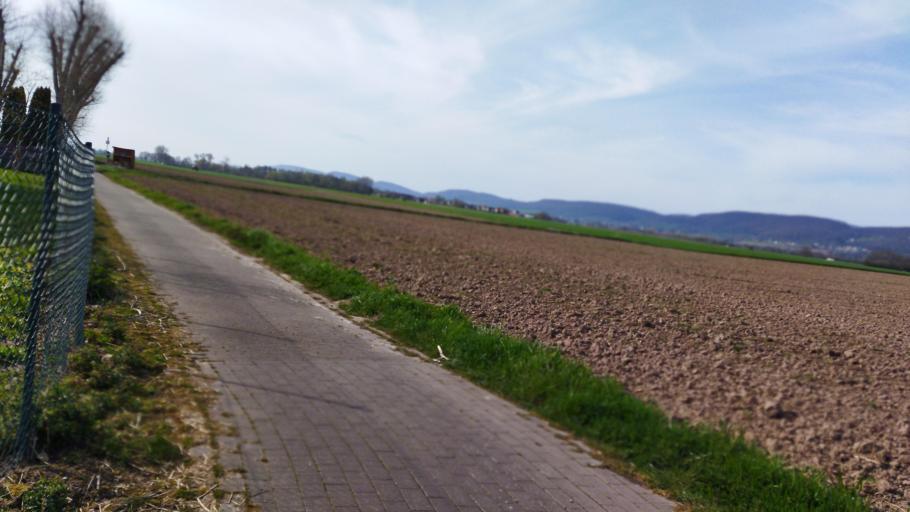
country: DE
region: Lower Saxony
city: Hessisch Oldendorf
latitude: 52.1634
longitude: 9.2127
